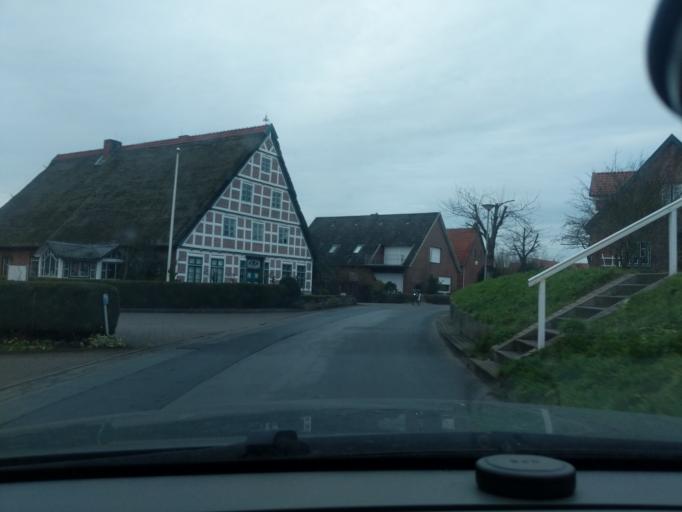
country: DE
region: Lower Saxony
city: Mittelnkirchen
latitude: 53.5337
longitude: 9.6125
